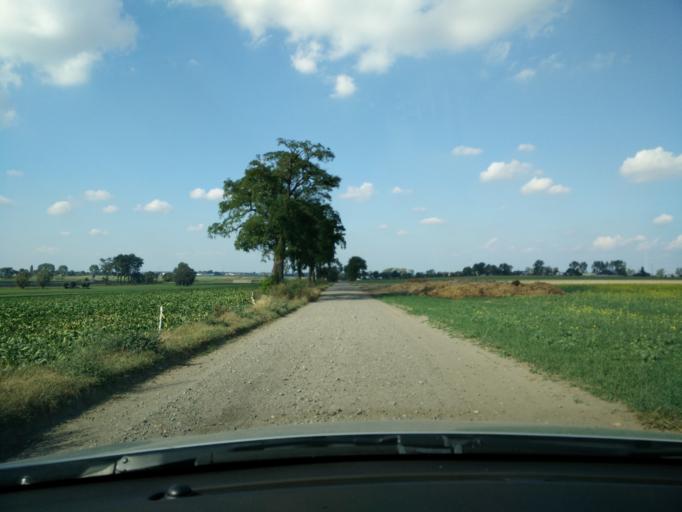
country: PL
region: Greater Poland Voivodeship
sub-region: Powiat poznanski
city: Kleszczewo
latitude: 52.2618
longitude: 17.1840
